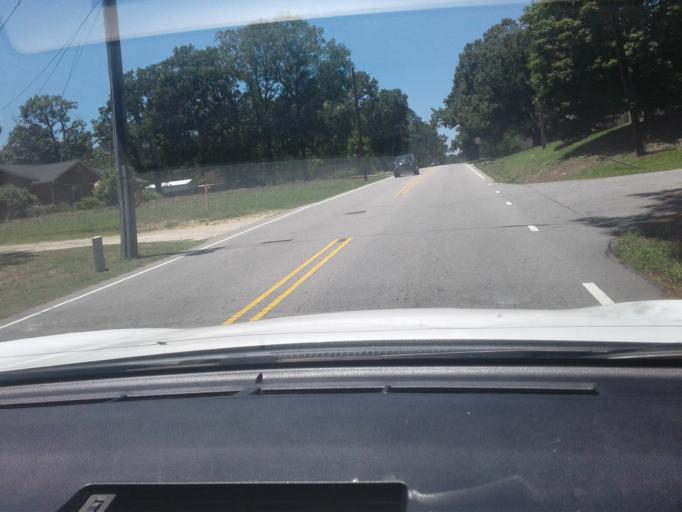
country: US
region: North Carolina
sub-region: Harnett County
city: Lillington
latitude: 35.3934
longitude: -78.8222
